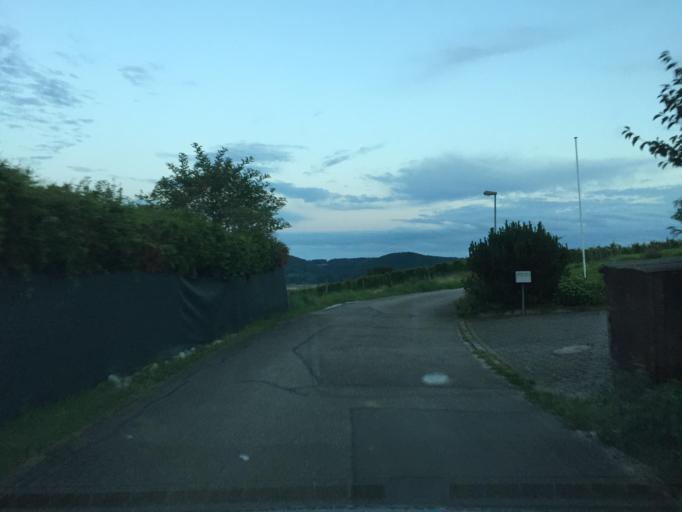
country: CH
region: Schaffhausen
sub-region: Bezirk Unterklettgau
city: Wilchingen
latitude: 47.6669
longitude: 8.4272
